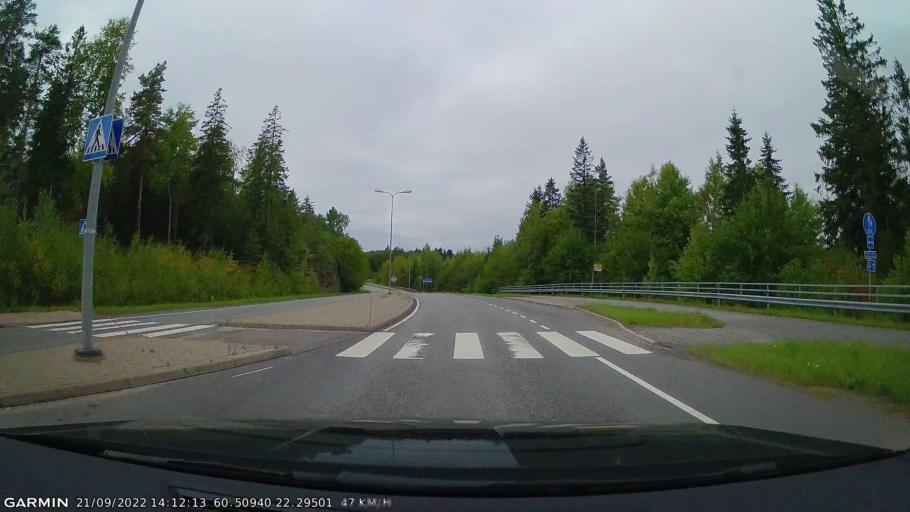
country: FI
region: Varsinais-Suomi
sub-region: Turku
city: Turku
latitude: 60.5092
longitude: 22.2953
